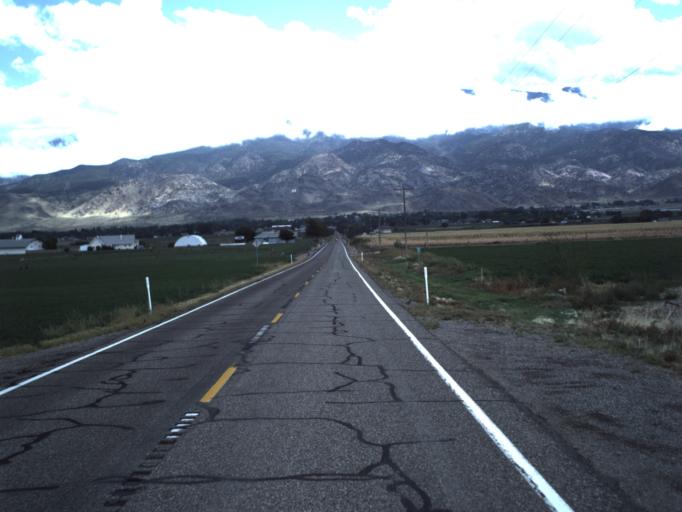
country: US
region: Utah
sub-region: Sevier County
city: Monroe
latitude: 38.6293
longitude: -112.1612
